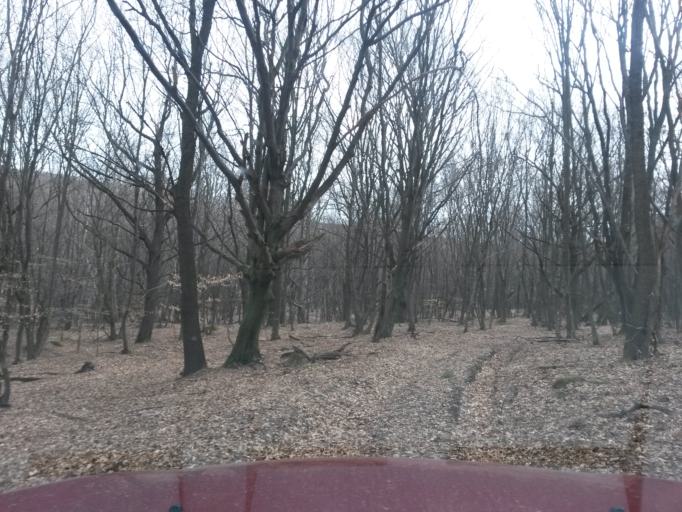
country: HU
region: Borsod-Abauj-Zemplen
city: Gonc
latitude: 48.5751
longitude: 21.3867
